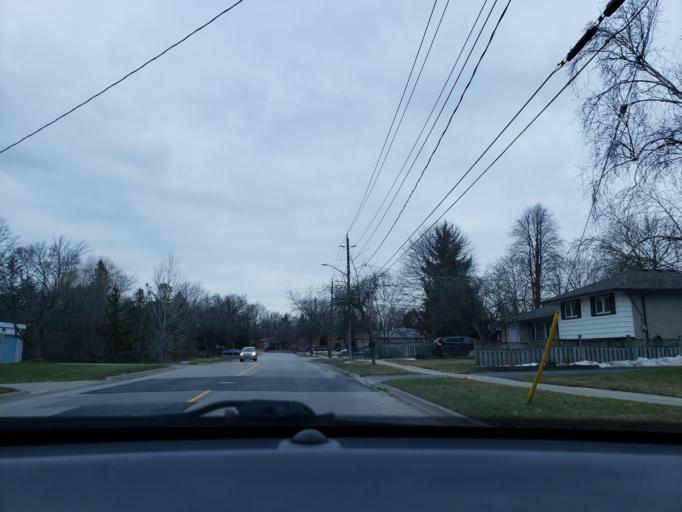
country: CA
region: Ontario
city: Newmarket
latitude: 44.0509
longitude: -79.4742
